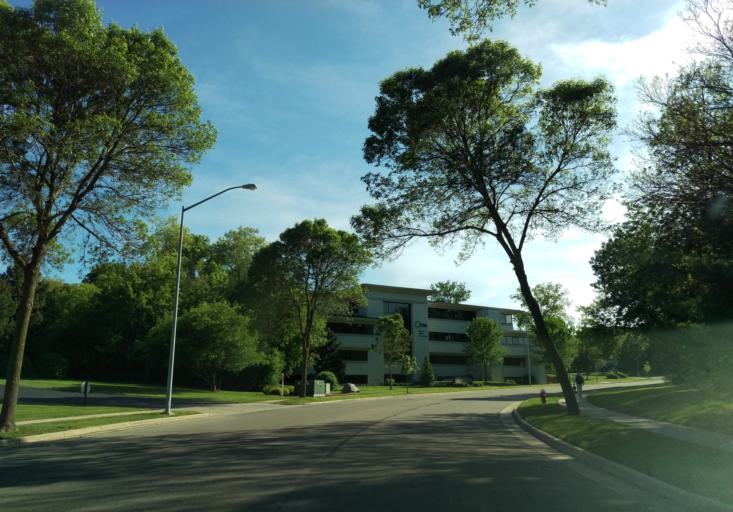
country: US
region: Wisconsin
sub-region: Dane County
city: Middleton
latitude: 43.0772
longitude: -89.5298
